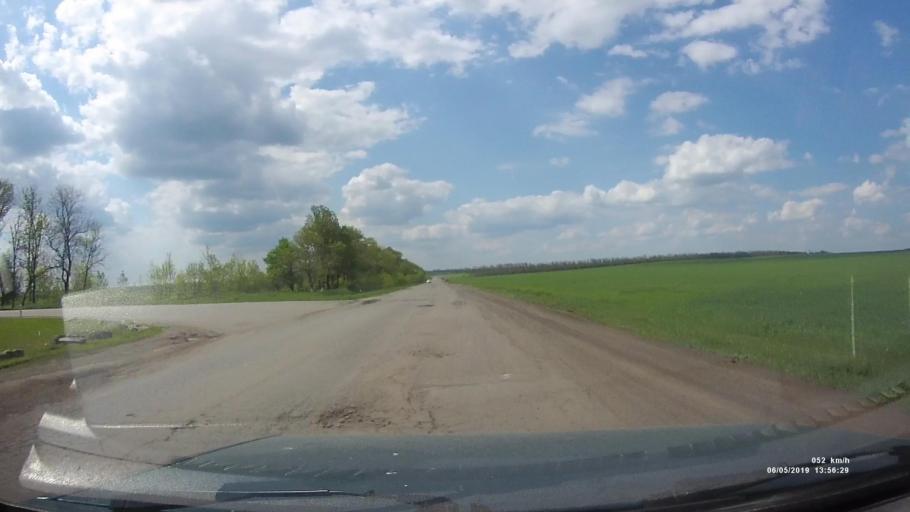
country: RU
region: Rostov
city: Melikhovskaya
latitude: 47.6809
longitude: 40.4306
